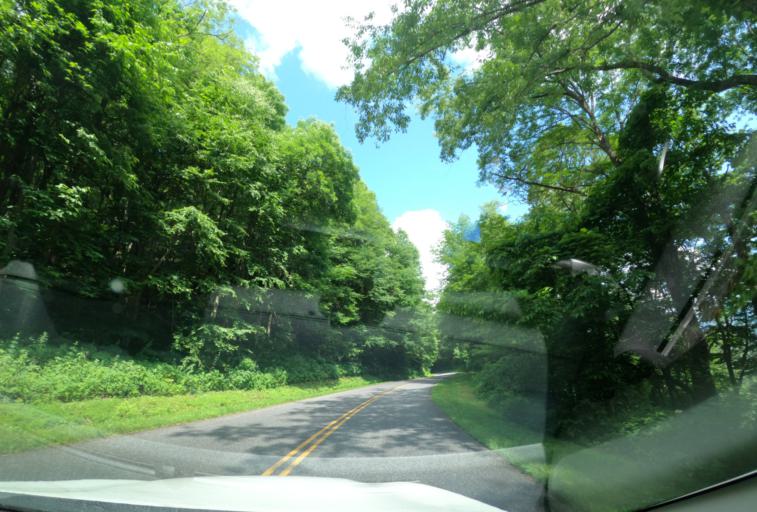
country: US
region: North Carolina
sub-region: Haywood County
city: Hazelwood
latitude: 35.4334
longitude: -83.0408
